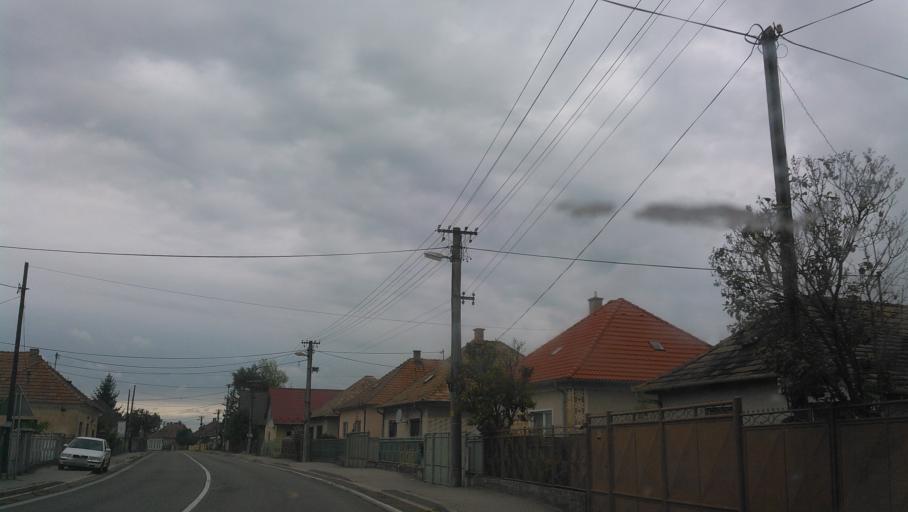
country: SK
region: Trnavsky
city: Dunajska Streda
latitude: 47.9762
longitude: 17.6624
